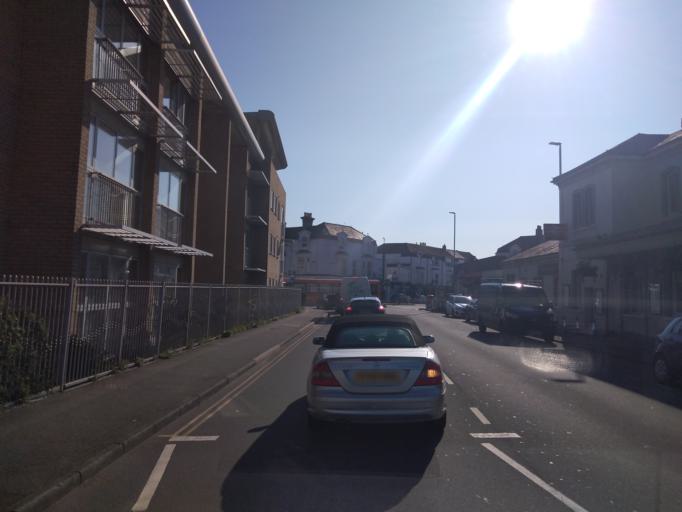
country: GB
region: England
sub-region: East Sussex
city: Seaford
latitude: 50.7732
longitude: 0.0999
